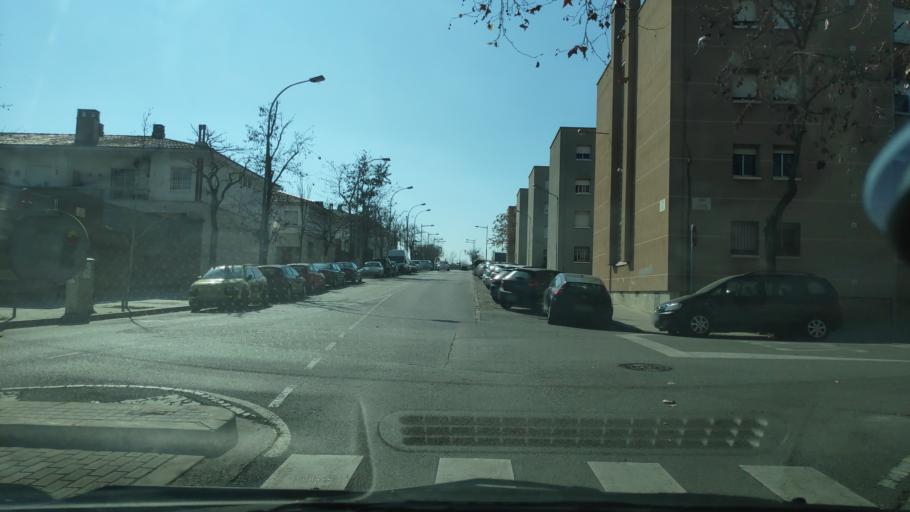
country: ES
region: Catalonia
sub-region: Provincia de Barcelona
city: Sant Quirze del Valles
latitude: 41.5419
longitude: 2.0904
